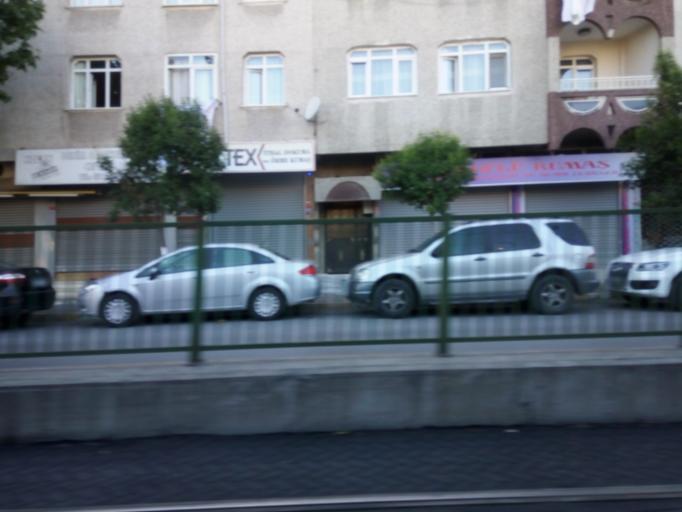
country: TR
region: Istanbul
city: Zeytinburnu
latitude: 41.0067
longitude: 28.9089
